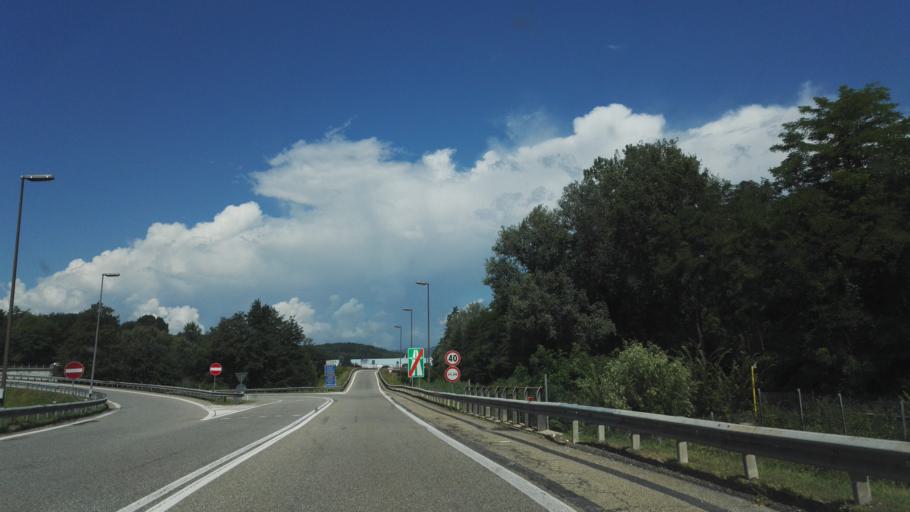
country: IT
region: Lombardy
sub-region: Provincia di Varese
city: Lisanza
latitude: 45.7147
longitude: 8.5944
